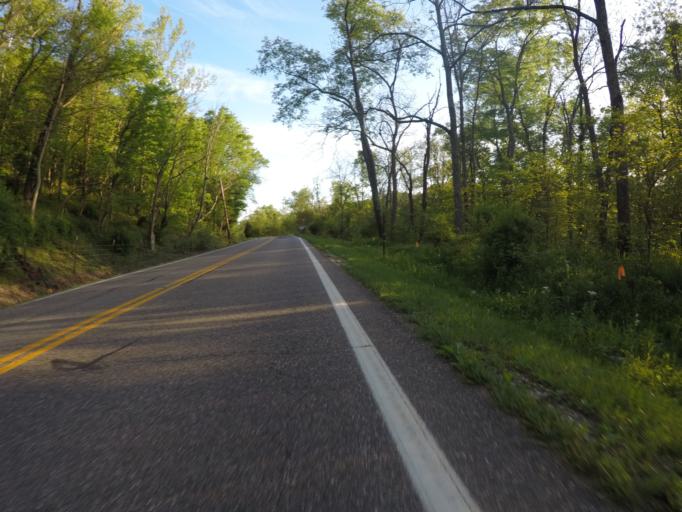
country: US
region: West Virginia
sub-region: Cabell County
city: Huntington
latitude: 38.5178
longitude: -82.4742
